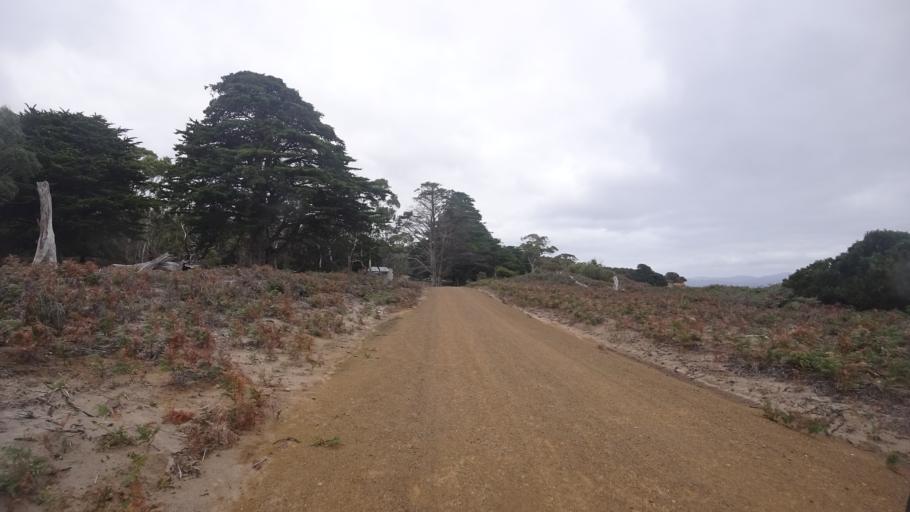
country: AU
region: Tasmania
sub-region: Sorell
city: Sorell
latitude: -42.5902
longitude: 148.0555
